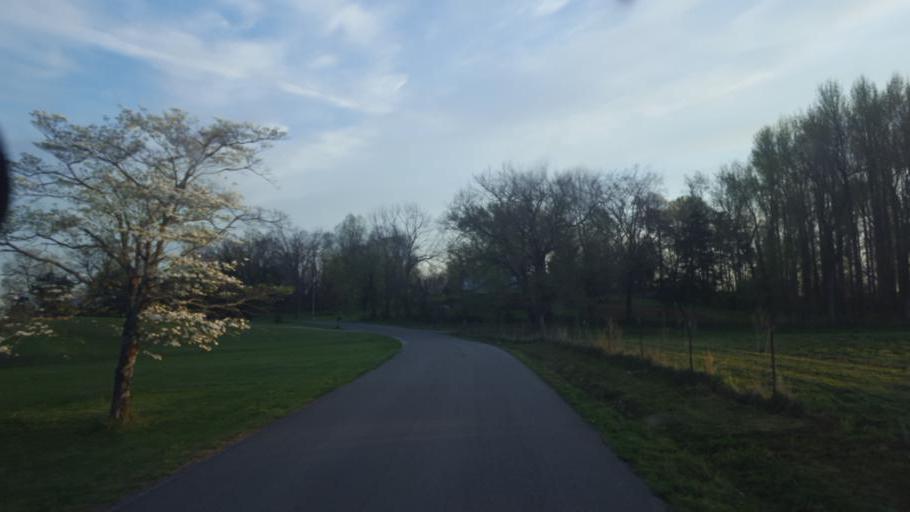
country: US
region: Kentucky
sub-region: Barren County
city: Cave City
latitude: 37.1356
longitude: -86.0243
